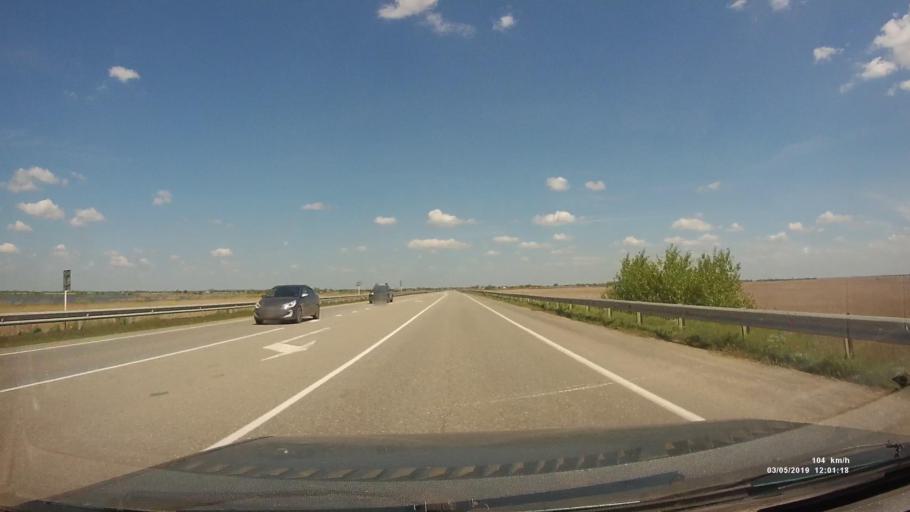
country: RU
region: Rostov
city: Bagayevskaya
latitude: 47.2611
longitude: 40.3496
